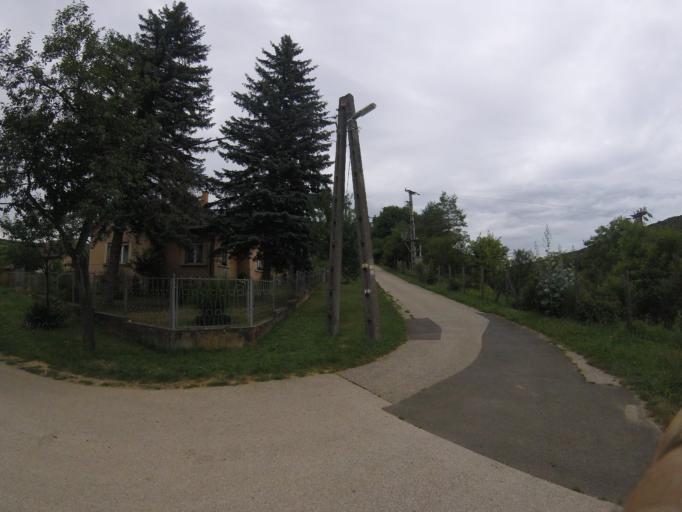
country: HU
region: Nograd
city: Romhany
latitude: 47.8715
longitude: 19.2476
